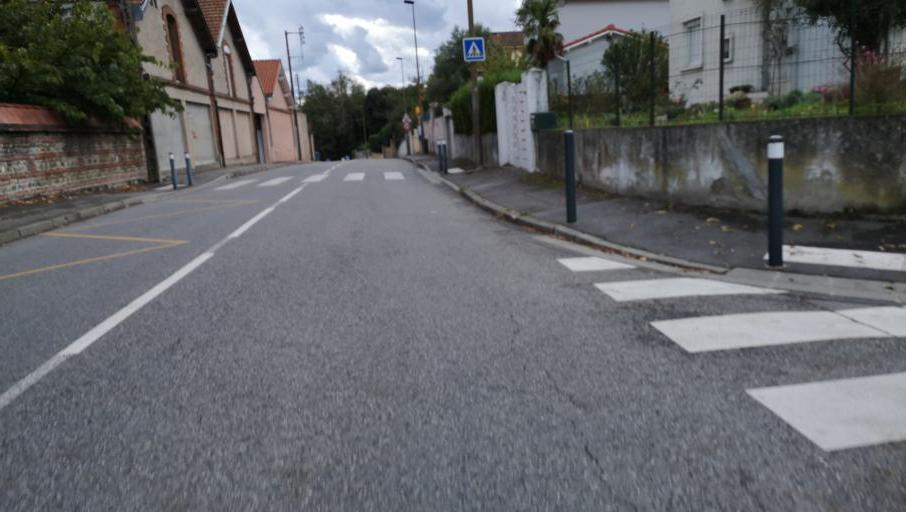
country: FR
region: Midi-Pyrenees
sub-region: Departement de la Haute-Garonne
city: Blagnac
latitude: 43.6157
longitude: 1.3994
